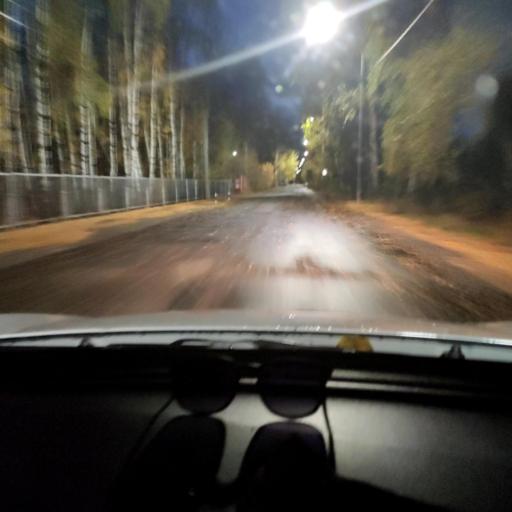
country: RU
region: Tatarstan
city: Verkhniy Uslon
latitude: 55.6017
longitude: 49.0214
